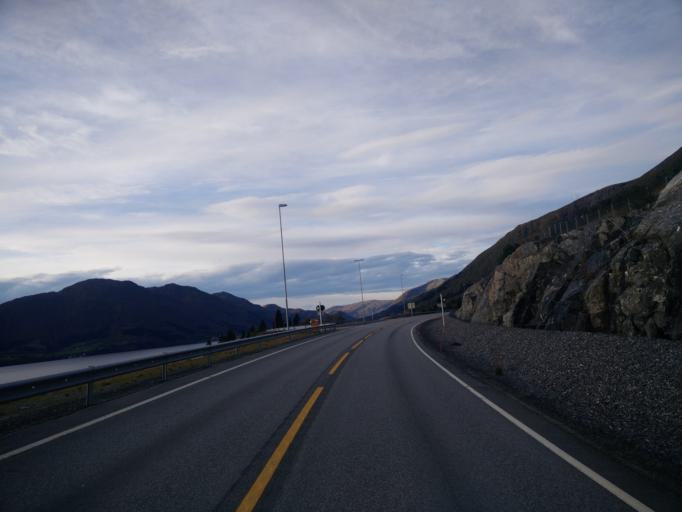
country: NO
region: More og Romsdal
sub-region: Gjemnes
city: Batnfjordsora
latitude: 62.9539
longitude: 7.7690
